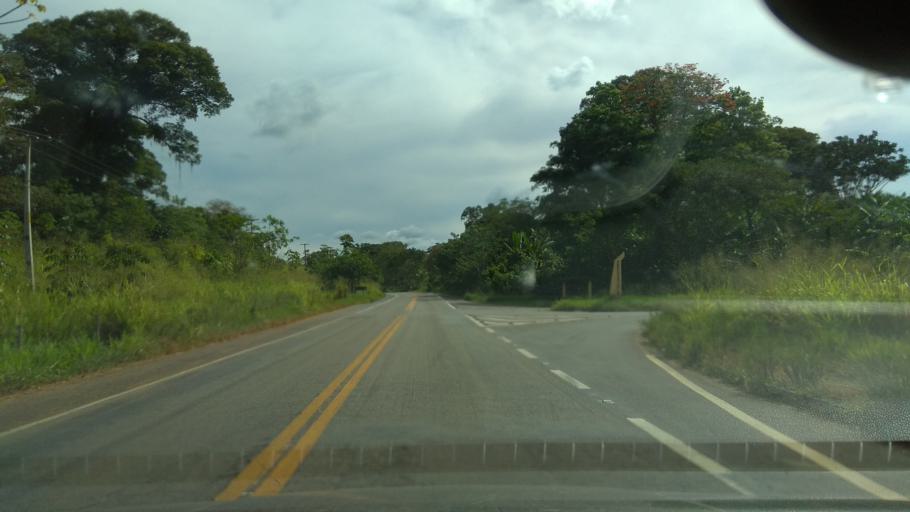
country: BR
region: Bahia
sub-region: Ubata
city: Ubata
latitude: -14.2291
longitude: -39.4464
